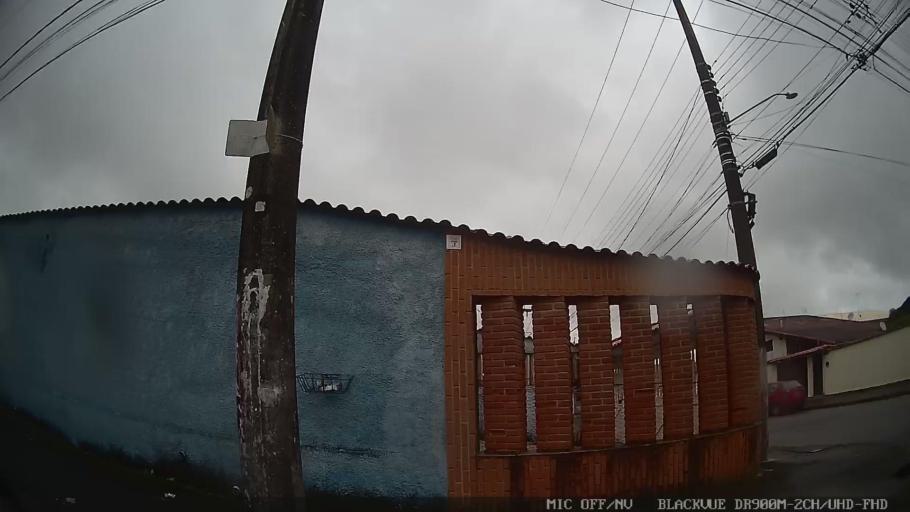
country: BR
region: Sao Paulo
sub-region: Itanhaem
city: Itanhaem
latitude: -24.1745
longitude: -46.7762
